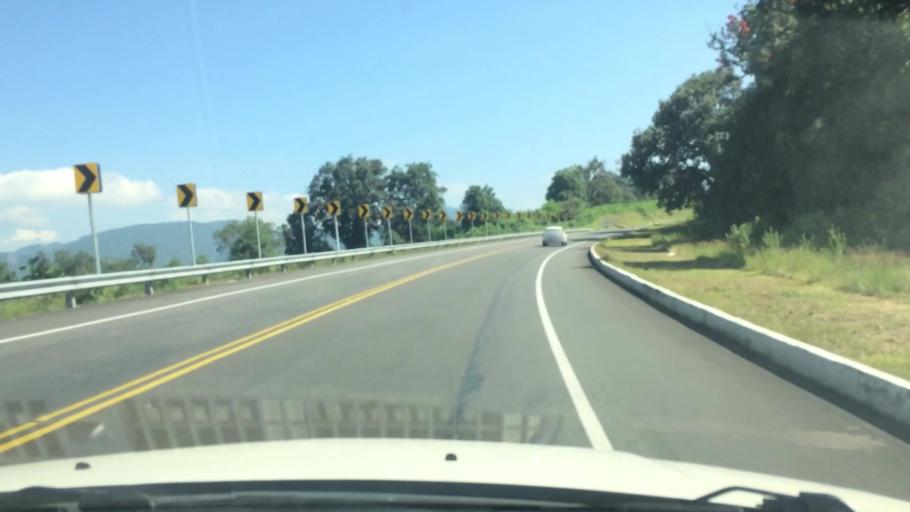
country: MX
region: Mexico
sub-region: Valle de Bravo
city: Colonia Rincon Villa del Valle
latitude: 19.2166
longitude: -100.0992
